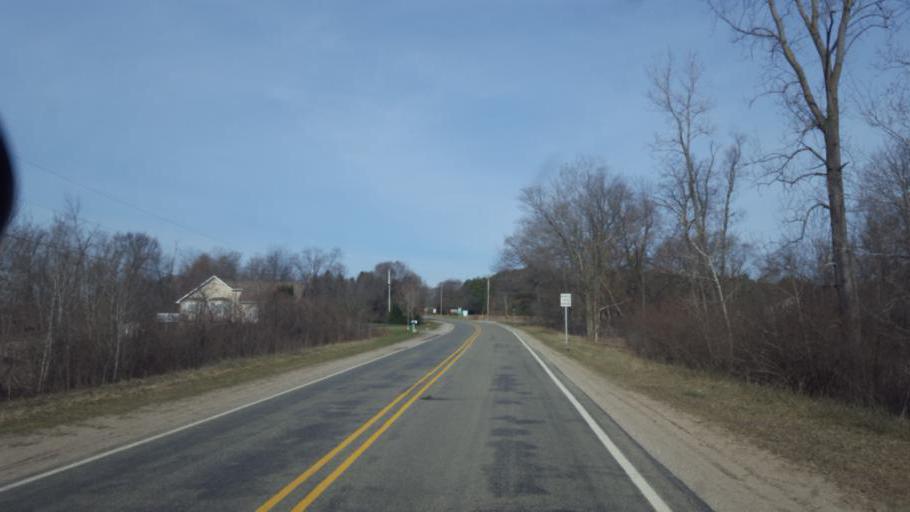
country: US
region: Michigan
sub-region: Montcalm County
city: Howard City
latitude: 43.4905
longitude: -85.4324
